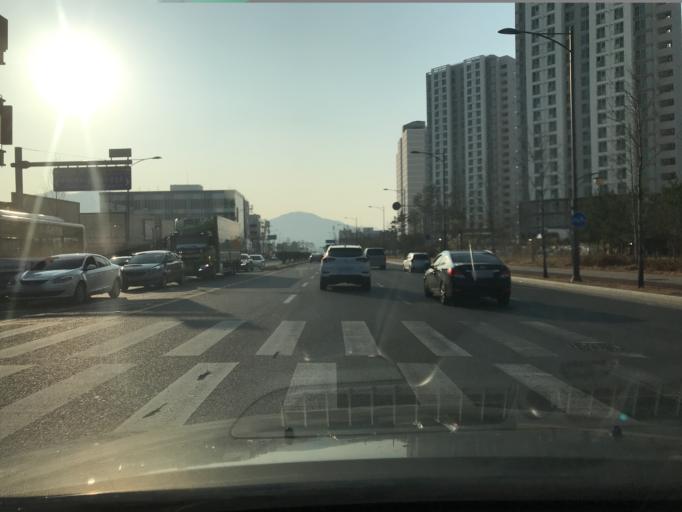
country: KR
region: Daegu
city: Hwawon
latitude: 35.6892
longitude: 128.4531
